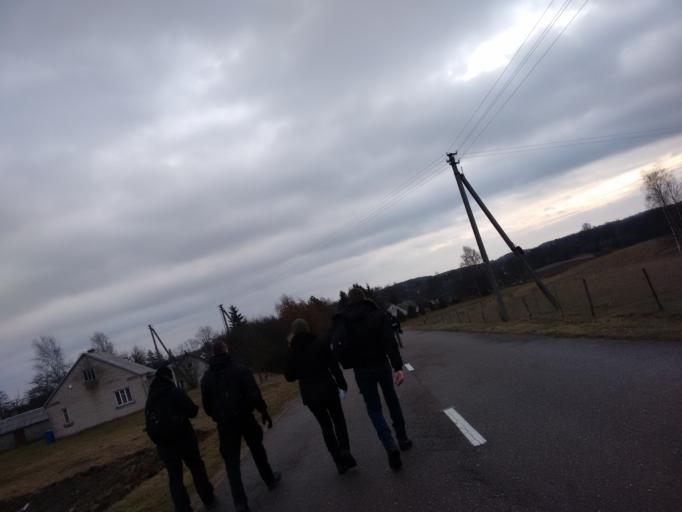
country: LT
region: Alytaus apskritis
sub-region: Alytus
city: Alytus
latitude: 54.2438
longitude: 23.8845
